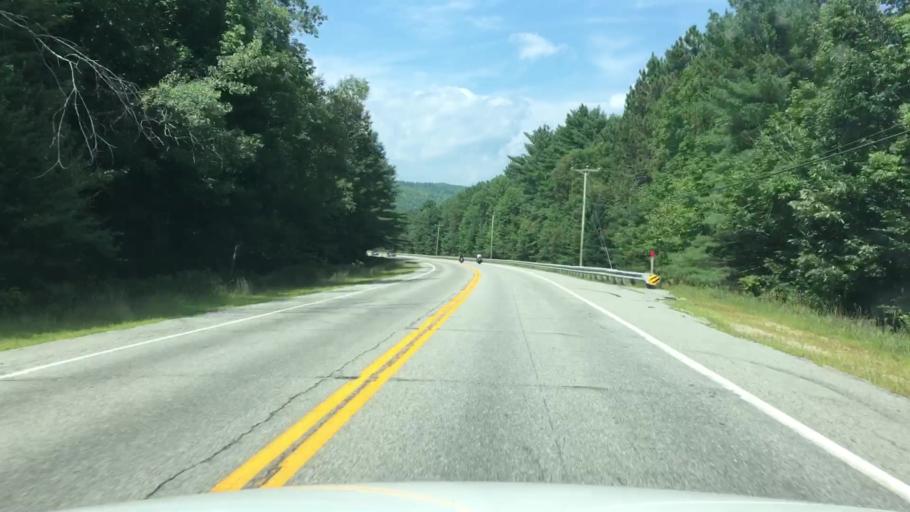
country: US
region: Maine
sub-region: Oxford County
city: Peru
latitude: 44.5079
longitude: -70.4062
